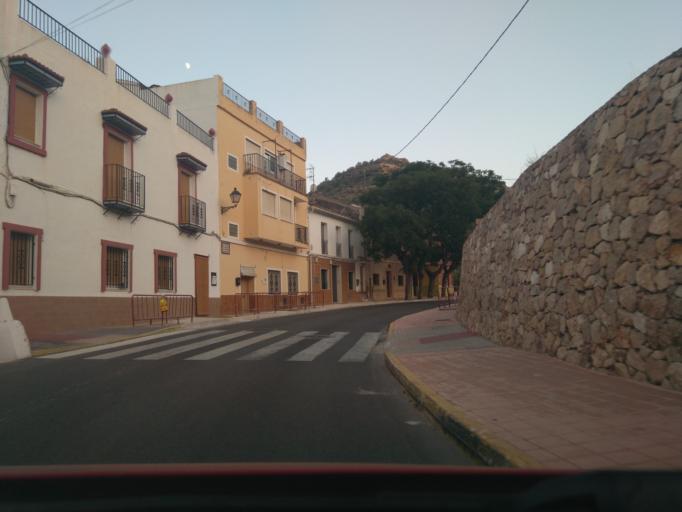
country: ES
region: Valencia
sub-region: Provincia de Valencia
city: Sumacarcer
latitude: 39.0923
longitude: -0.6284
